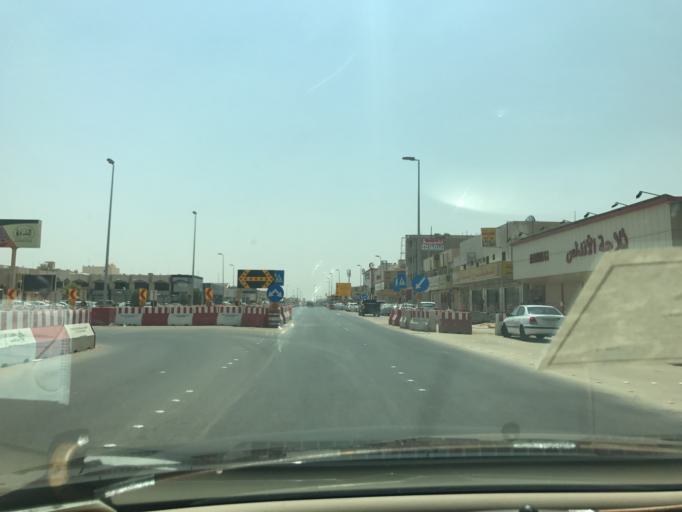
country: SA
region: Ar Riyad
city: Riyadh
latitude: 24.7492
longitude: 46.7728
